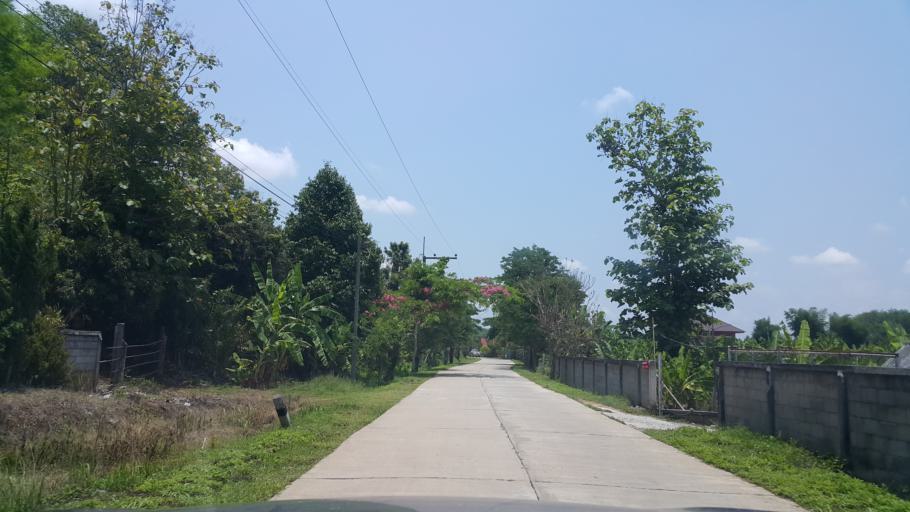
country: TH
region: Chiang Rai
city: Chiang Rai
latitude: 19.9766
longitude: 99.7542
